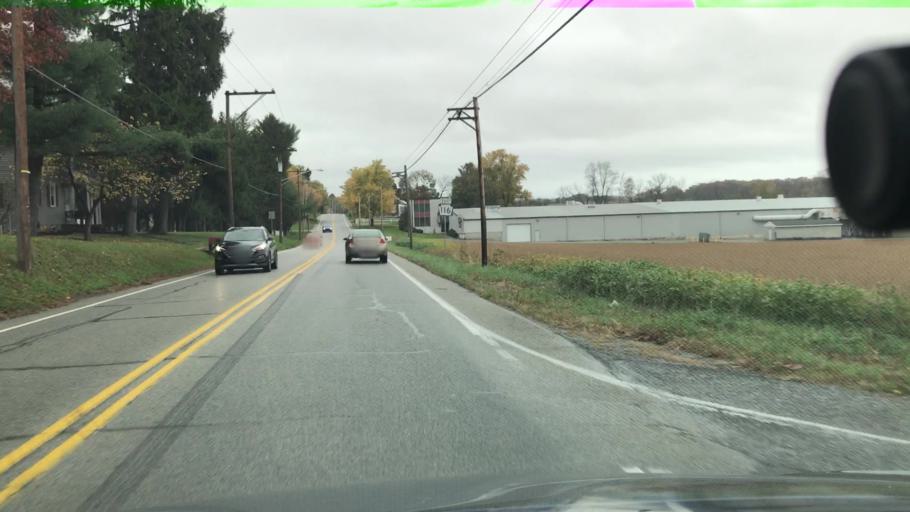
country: US
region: Pennsylvania
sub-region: York County
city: Spring Grove
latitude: 39.9130
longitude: -76.8392
